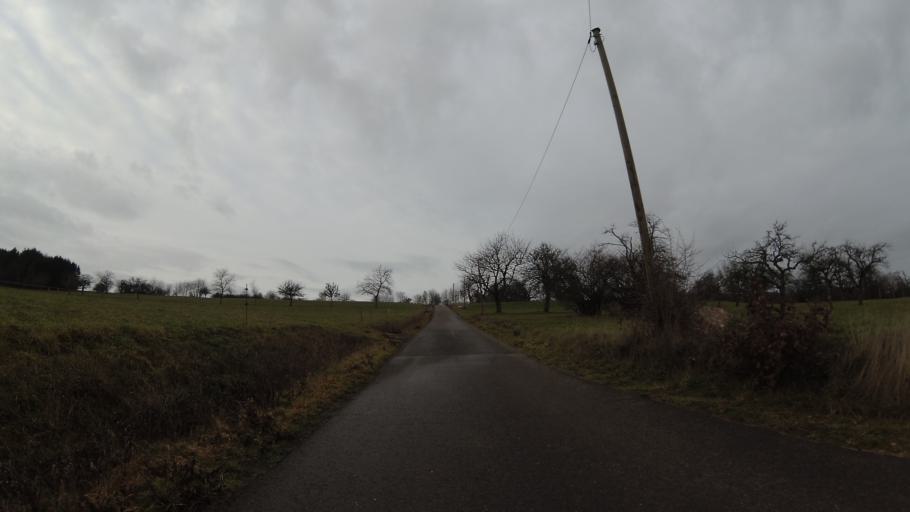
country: DE
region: Rheinland-Pfalz
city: Breitenbach
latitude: 49.4427
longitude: 7.2765
